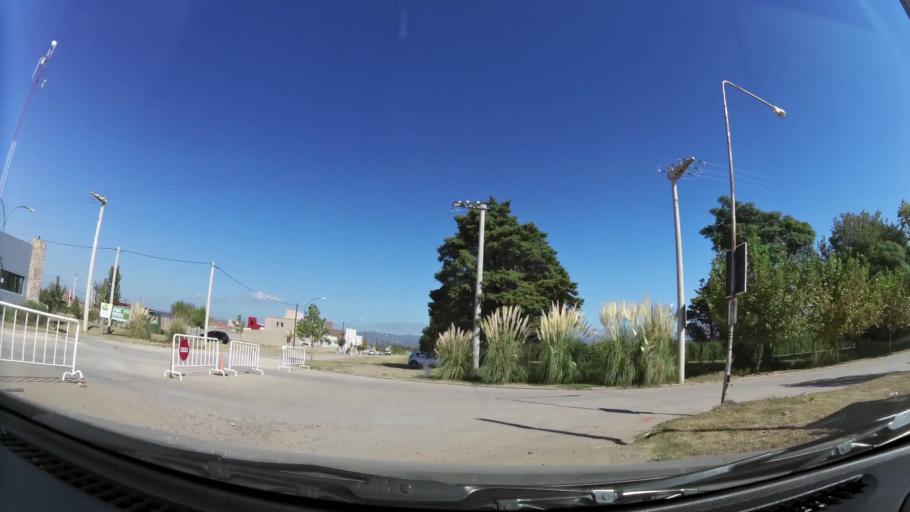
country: AR
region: Cordoba
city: Villa Allende
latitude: -31.3084
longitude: -64.2649
